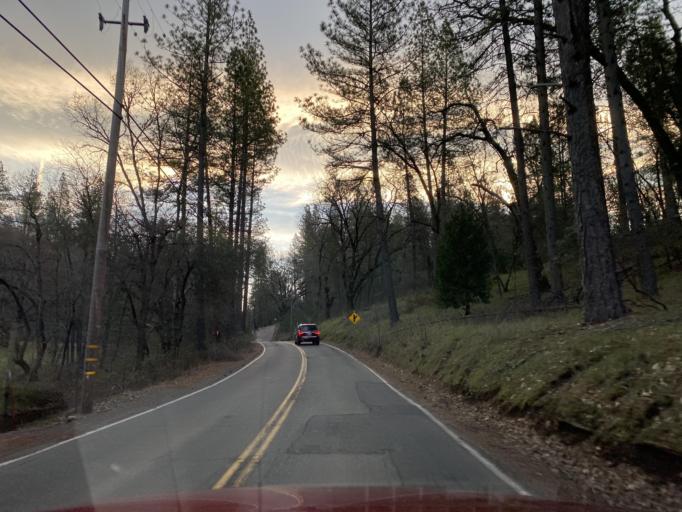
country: US
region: California
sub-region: Amador County
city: Pine Grove
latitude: 38.4968
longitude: -120.7252
